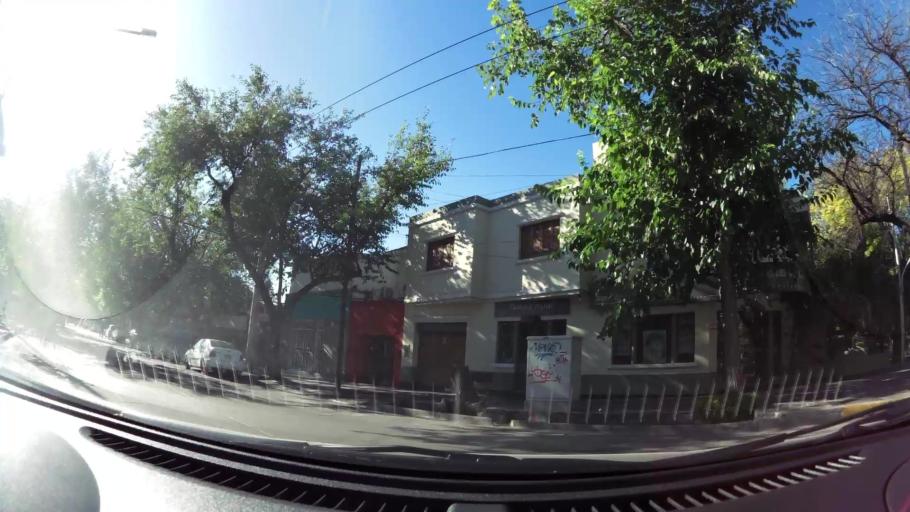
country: AR
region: Mendoza
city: Las Heras
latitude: -32.8690
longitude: -68.8536
